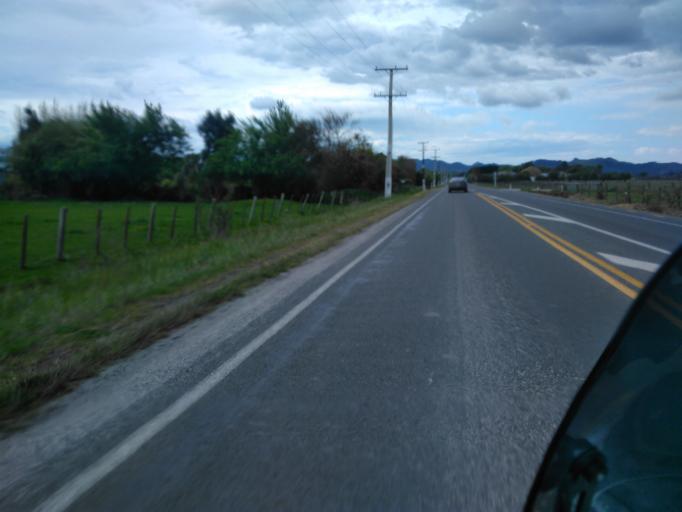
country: NZ
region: Gisborne
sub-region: Gisborne District
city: Gisborne
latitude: -38.6542
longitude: 177.9546
